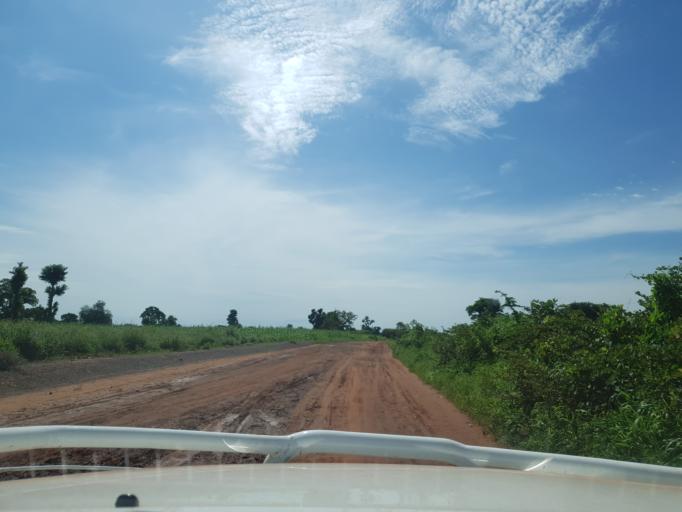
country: ML
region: Koulikoro
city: Banamba
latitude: 13.2797
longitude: -7.5512
